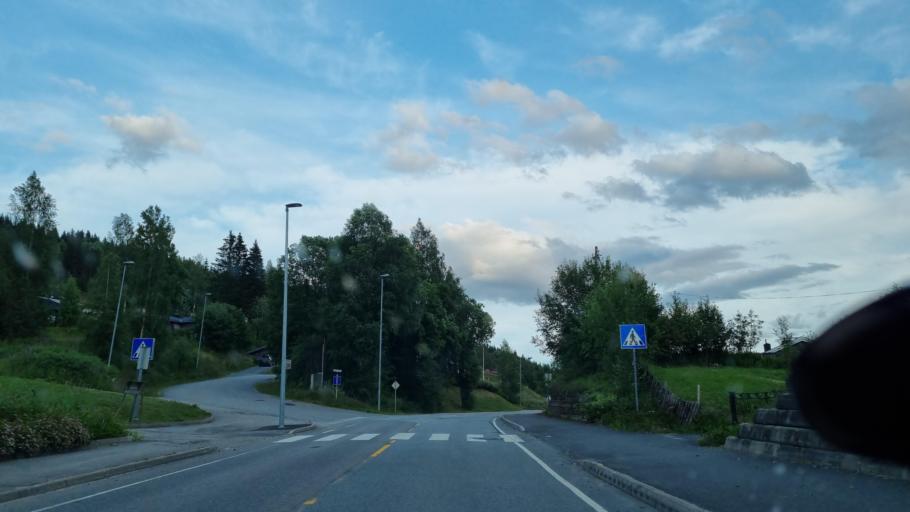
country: NO
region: Hedmark
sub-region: Trysil
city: Innbygda
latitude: 61.3111
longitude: 12.2704
